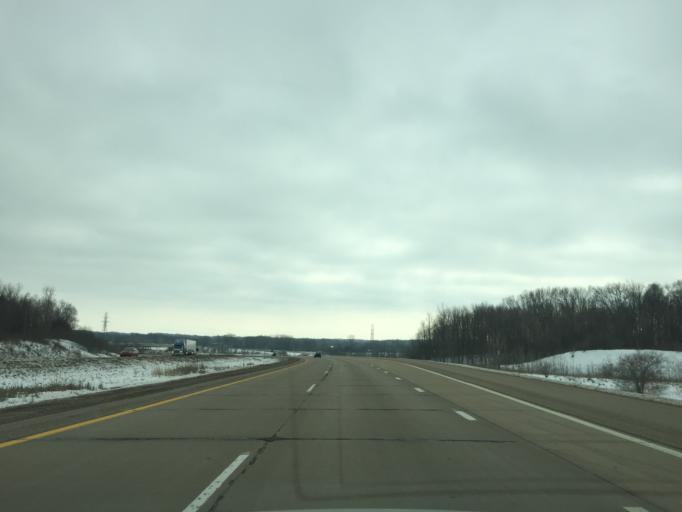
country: US
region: Michigan
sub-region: Ottawa County
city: Hudsonville
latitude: 42.8513
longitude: -85.8100
